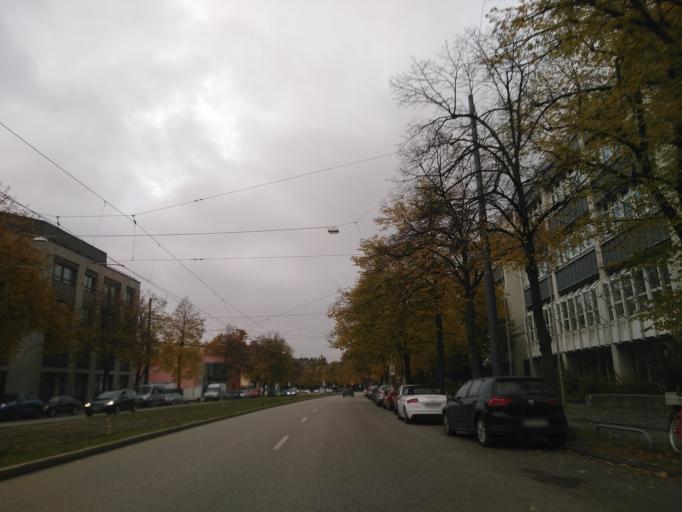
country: DE
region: Bavaria
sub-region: Upper Bavaria
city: Munich
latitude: 48.1132
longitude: 11.5930
